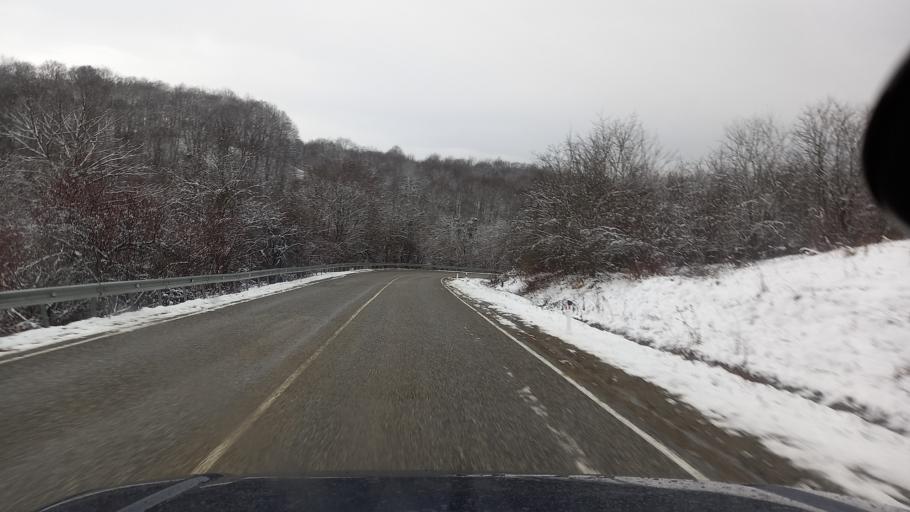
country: RU
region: Adygeya
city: Abadzekhskaya
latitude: 44.3515
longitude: 40.3262
